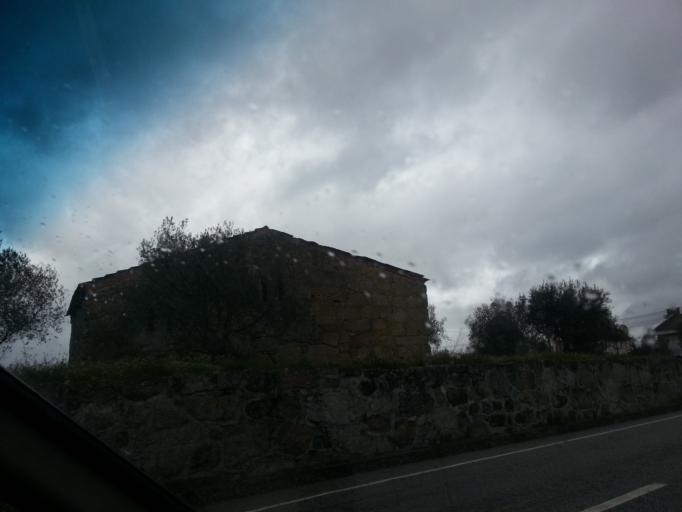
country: PT
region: Viseu
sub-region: Viseu
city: Rio de Loba
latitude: 40.6290
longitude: -7.8644
